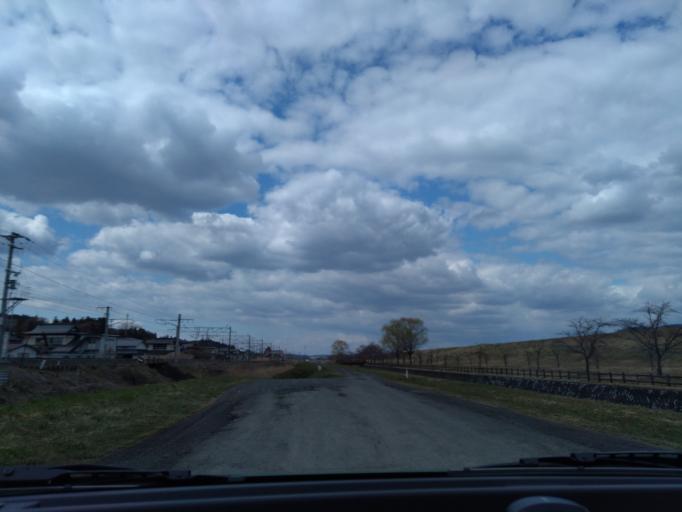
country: JP
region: Iwate
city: Ichinoseki
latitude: 38.9475
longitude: 141.1338
